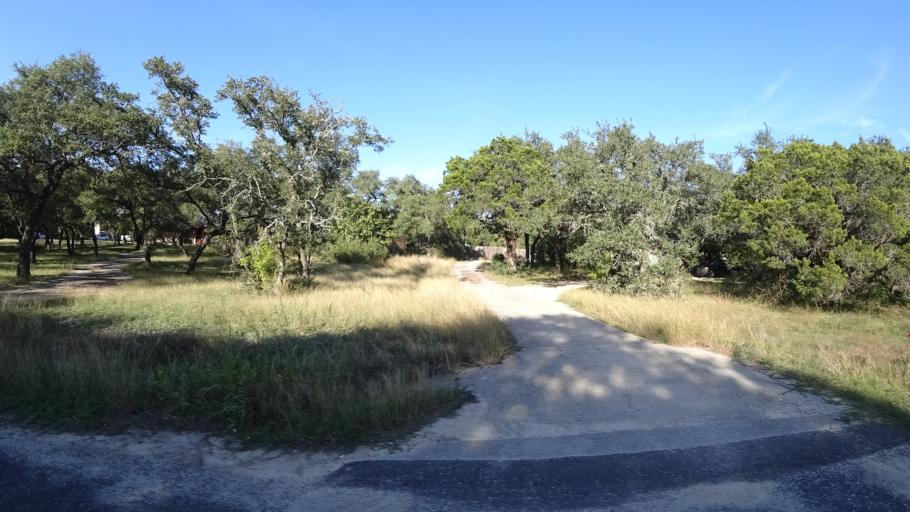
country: US
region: Texas
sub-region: Travis County
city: Barton Creek
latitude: 30.2457
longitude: -97.9126
